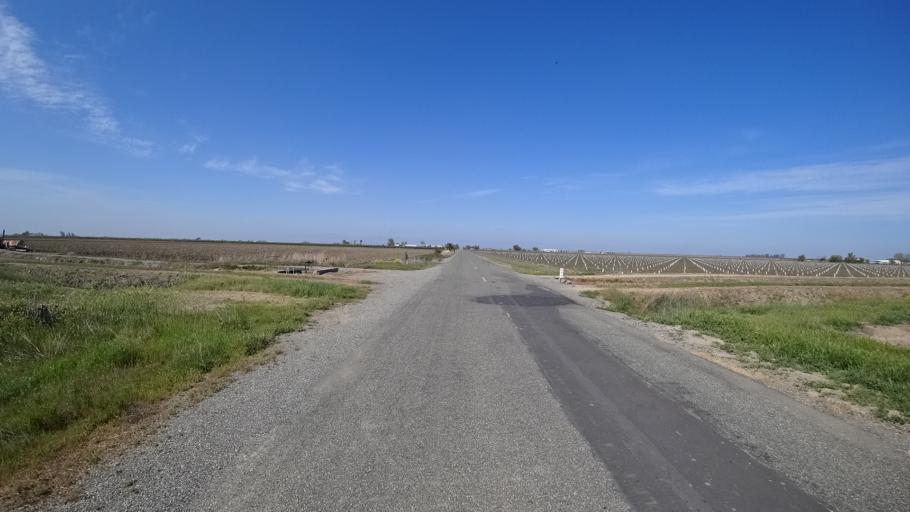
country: US
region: California
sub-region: Glenn County
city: Hamilton City
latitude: 39.6161
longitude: -122.0508
